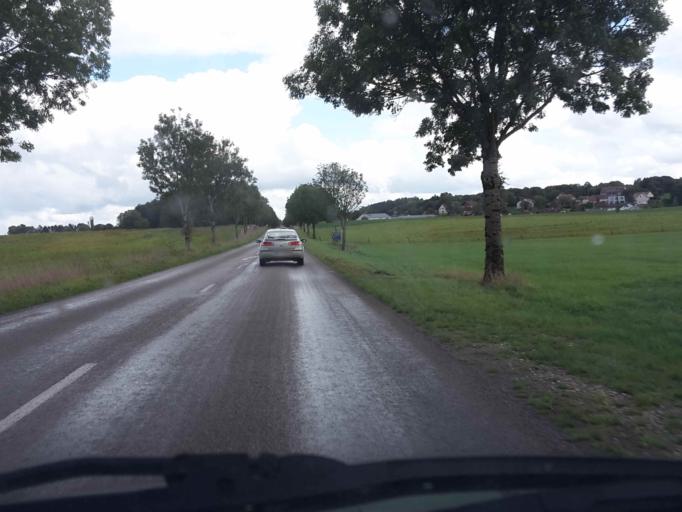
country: FR
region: Franche-Comte
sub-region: Departement du Doubs
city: Nancray
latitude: 47.2437
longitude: 6.1662
